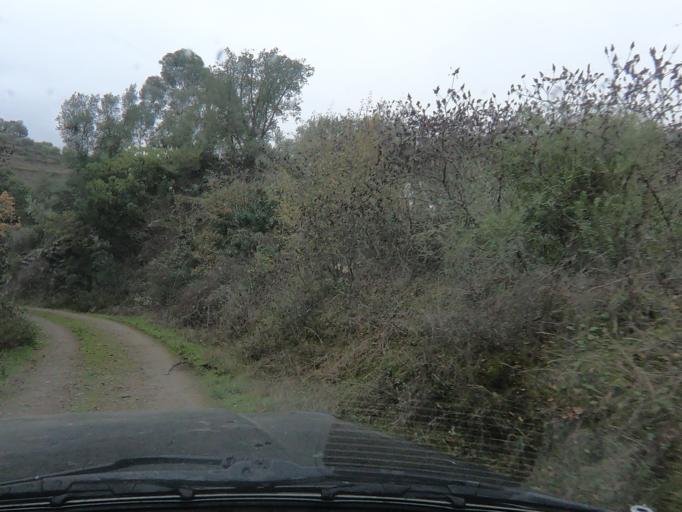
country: PT
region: Vila Real
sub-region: Santa Marta de Penaguiao
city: Santa Marta de Penaguiao
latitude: 41.2065
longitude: -7.7601
